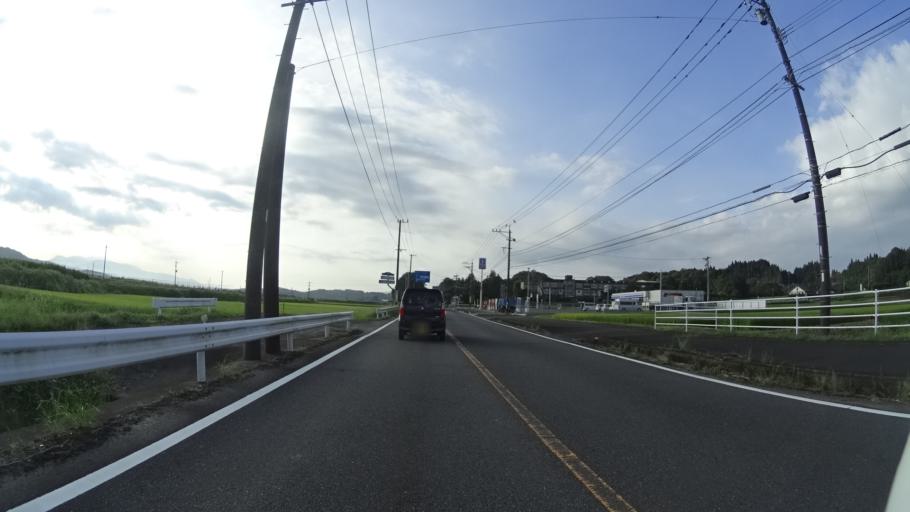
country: JP
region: Kagoshima
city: Okuchi-shinohara
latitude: 32.0256
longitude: 130.5955
